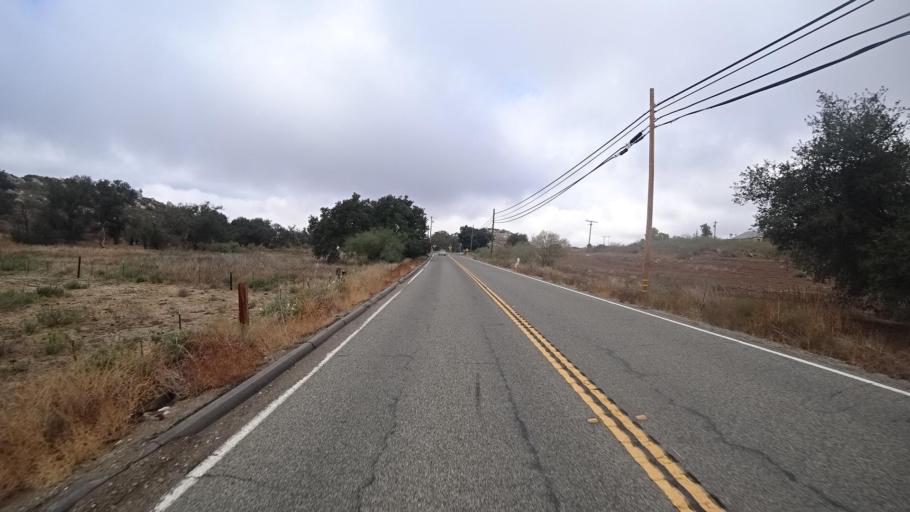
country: MX
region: Baja California
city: Tecate
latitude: 32.6003
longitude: -116.5884
